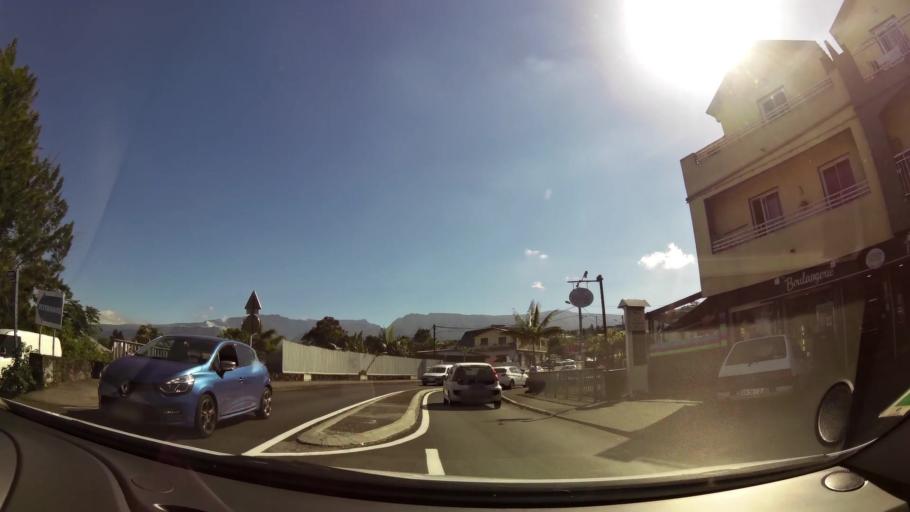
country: RE
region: Reunion
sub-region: Reunion
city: Le Tampon
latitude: -21.2650
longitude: 55.5079
